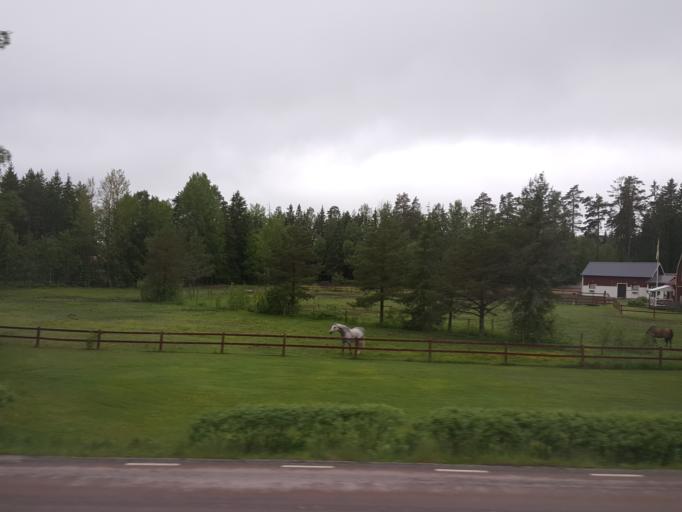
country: SE
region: Vaestmanland
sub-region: Sala Kommun
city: Sala
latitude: 59.9495
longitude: 16.5344
